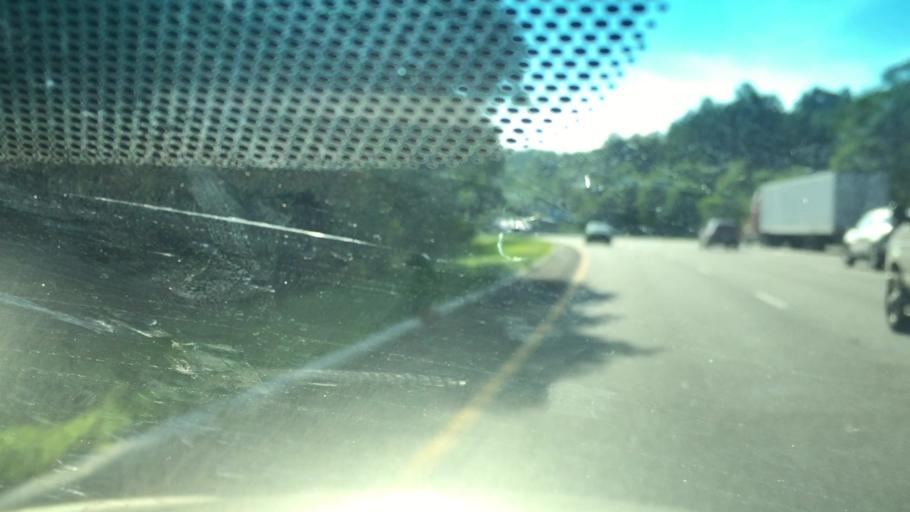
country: US
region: New Jersey
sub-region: Morris County
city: Budd Lake
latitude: 40.9253
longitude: -74.7854
